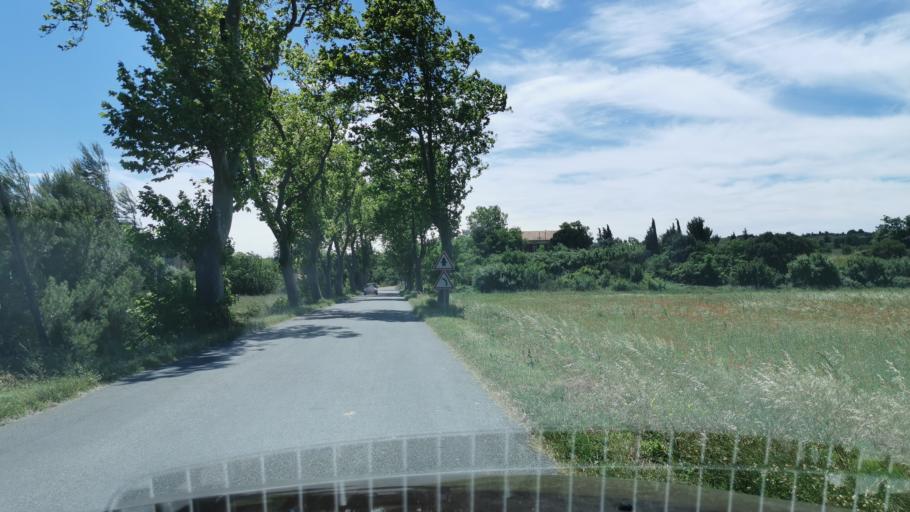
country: FR
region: Languedoc-Roussillon
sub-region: Departement de l'Aude
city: Marcorignan
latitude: 43.2156
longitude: 2.9280
